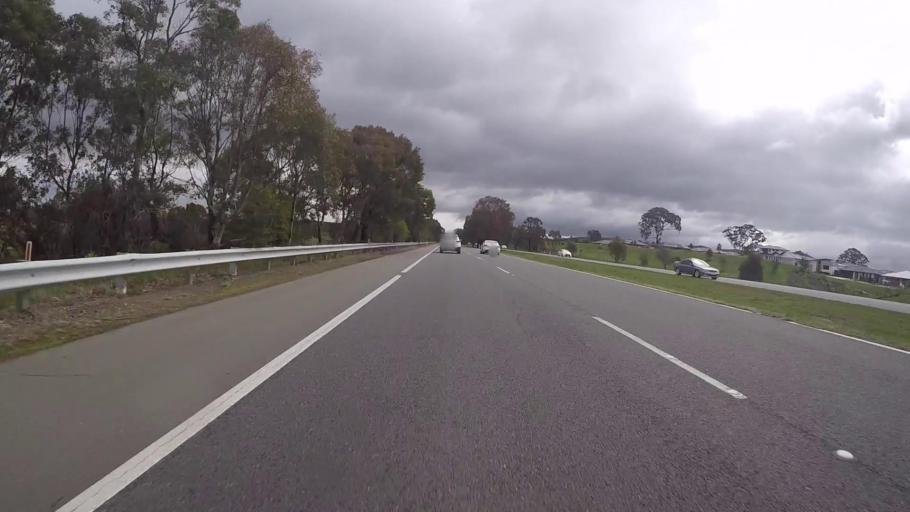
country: AU
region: Australian Capital Territory
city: Kaleen
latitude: -35.2091
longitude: 149.1074
